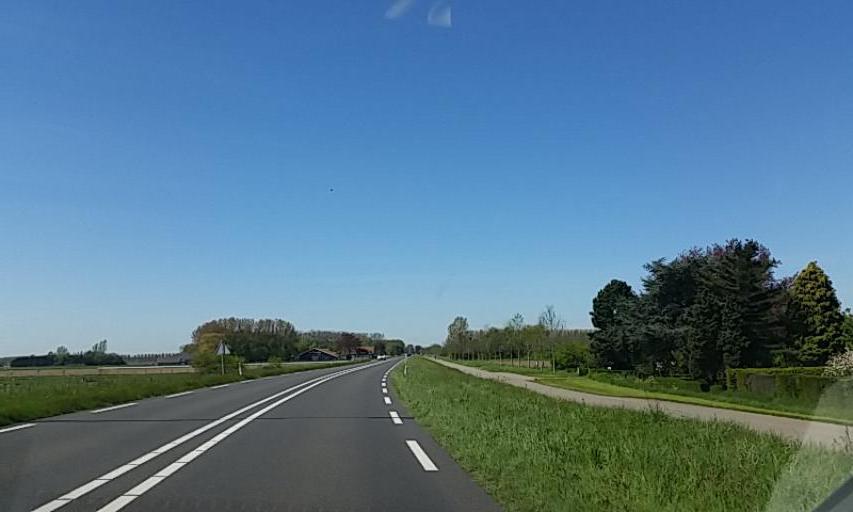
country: NL
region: Zeeland
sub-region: Gemeente Terneuzen
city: Koewacht
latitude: 51.2661
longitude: 3.9974
